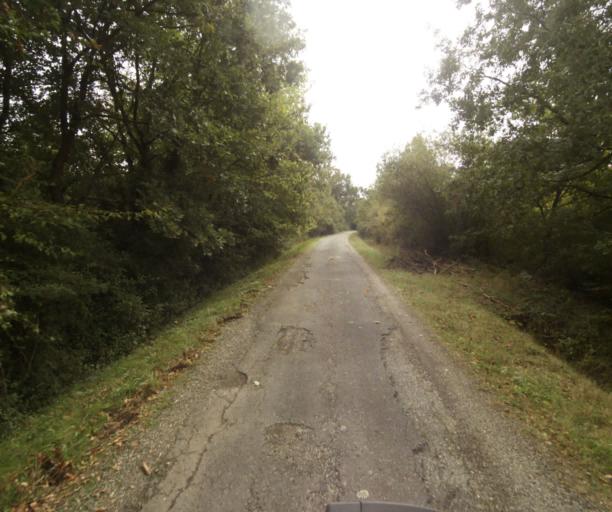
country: FR
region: Midi-Pyrenees
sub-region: Departement du Tarn-et-Garonne
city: Montech
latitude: 43.9765
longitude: 1.2512
